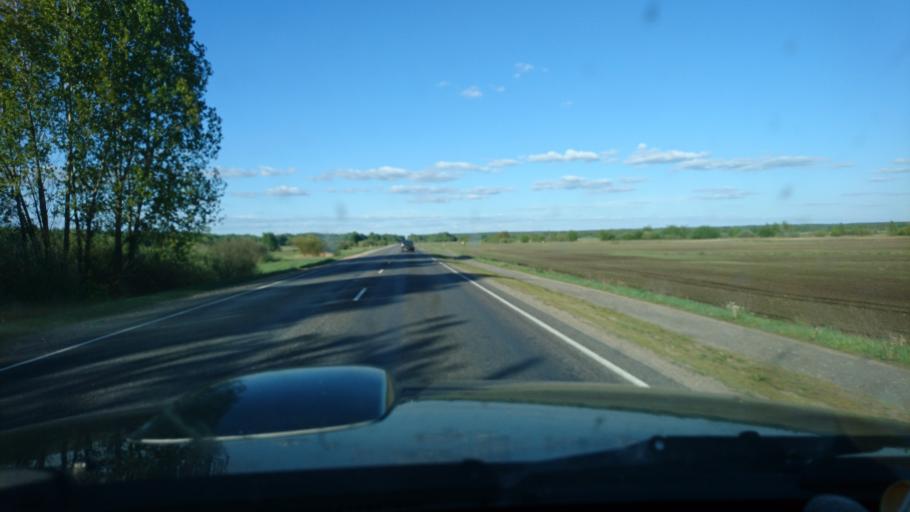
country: BY
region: Brest
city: Byaroza
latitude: 52.5495
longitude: 25.0151
